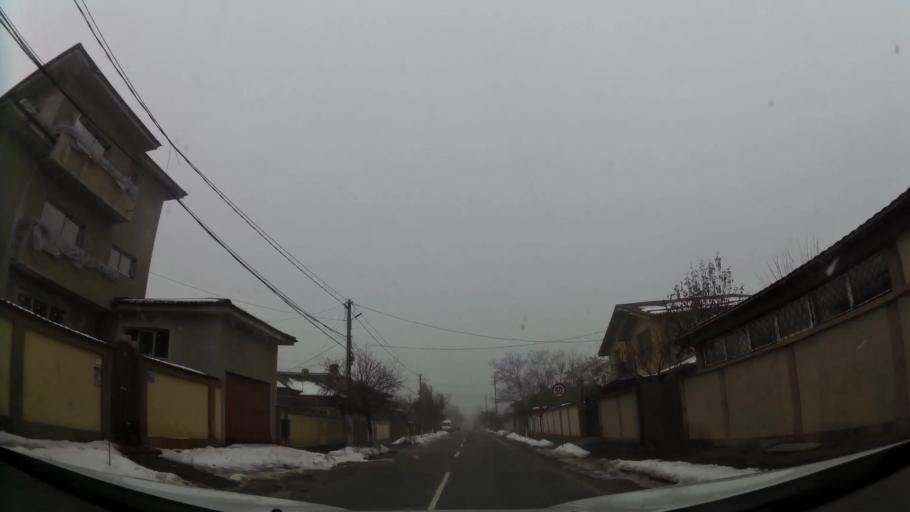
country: RO
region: Ilfov
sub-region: Comuna Chiajna
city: Chiajna
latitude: 44.4602
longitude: 25.9781
